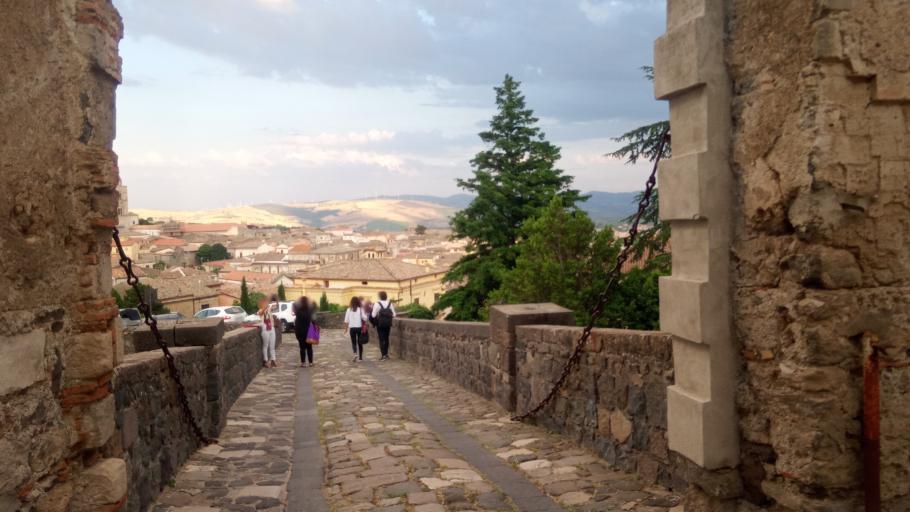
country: IT
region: Basilicate
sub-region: Provincia di Potenza
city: Melfi
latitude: 40.9982
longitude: 15.6534
